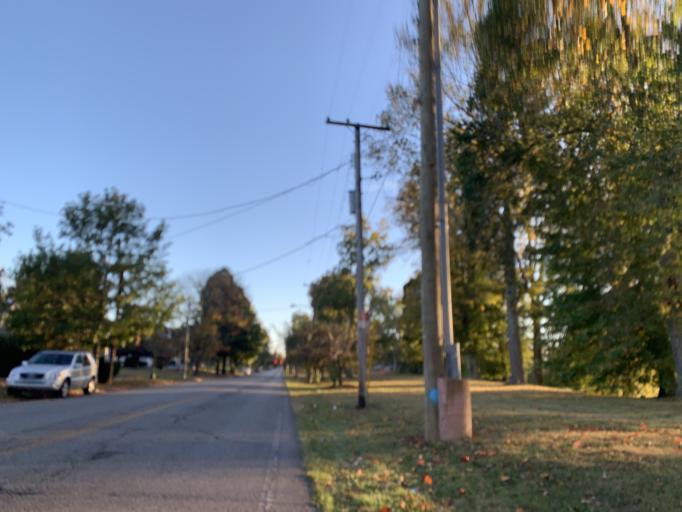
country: US
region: Indiana
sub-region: Floyd County
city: New Albany
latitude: 38.2540
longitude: -85.8268
